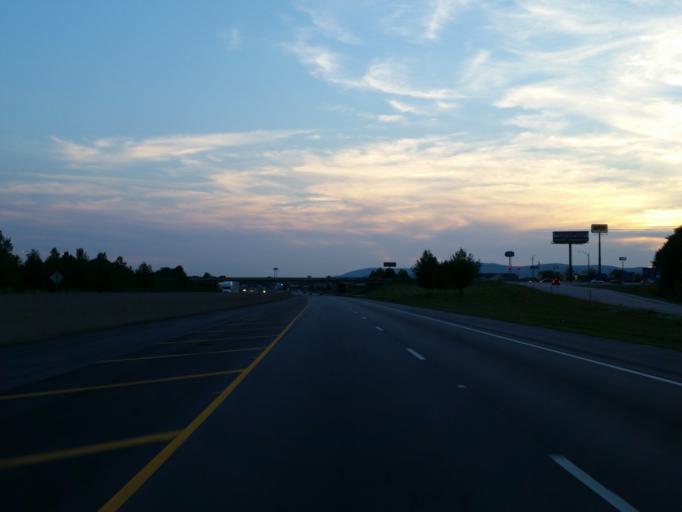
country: US
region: Alabama
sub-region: Calhoun County
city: Oxford
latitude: 33.6118
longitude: -85.7829
